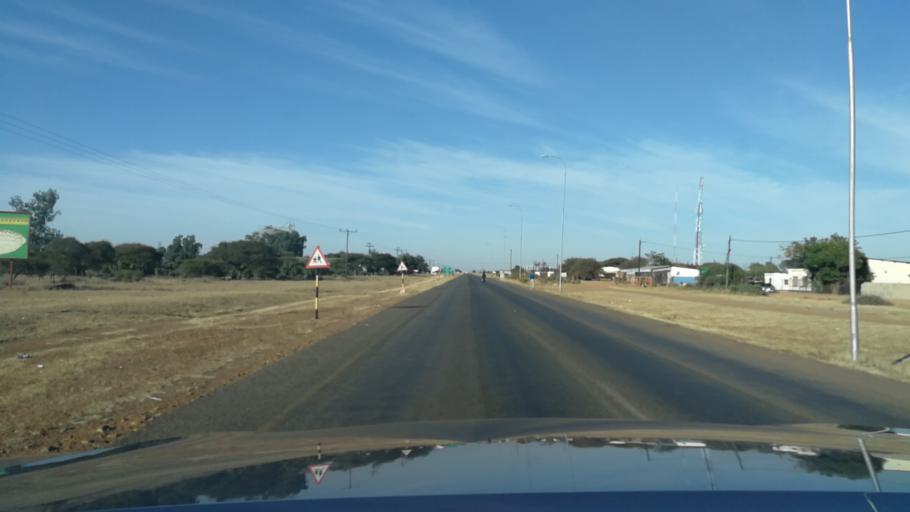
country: BW
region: South East
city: Janeng
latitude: -25.4689
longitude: 25.6003
